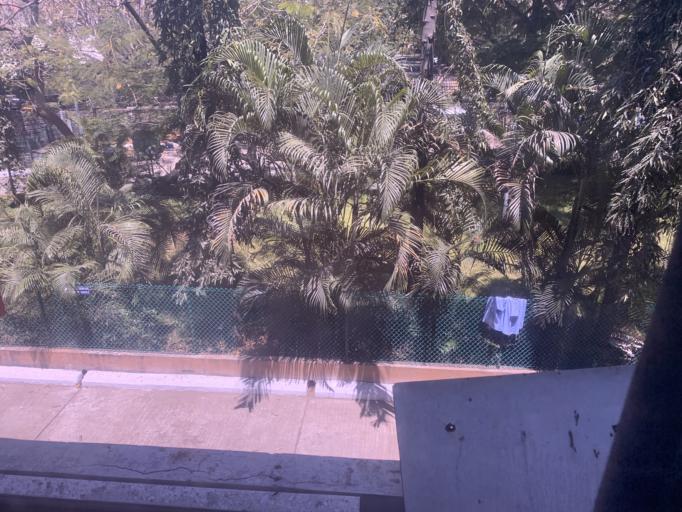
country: IN
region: Tamil Nadu
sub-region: Chennai
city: Gandhi Nagar
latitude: 13.0033
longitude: 80.2695
